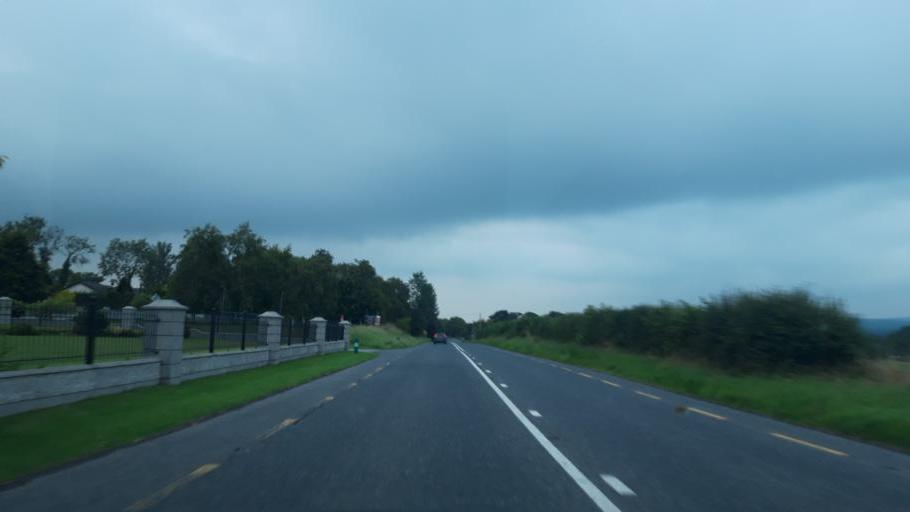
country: IE
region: Leinster
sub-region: Kilkenny
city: Thomastown
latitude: 52.5435
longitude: -7.1335
